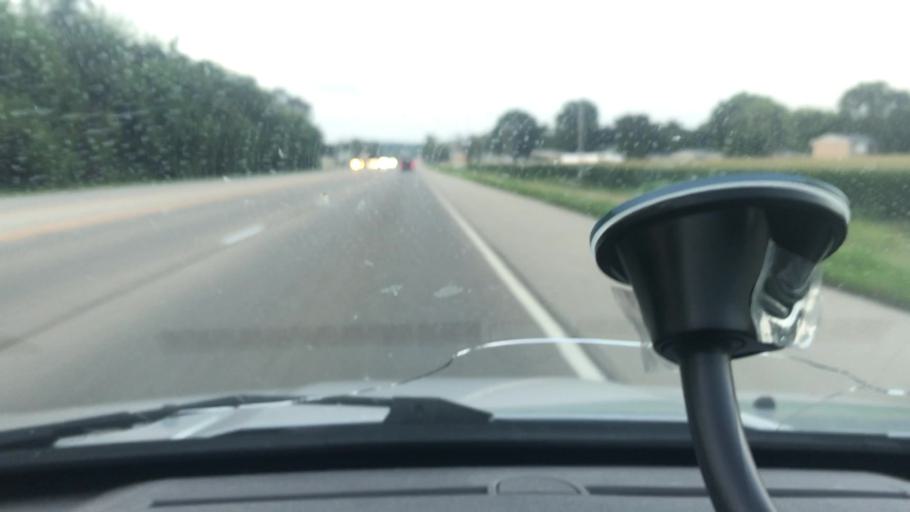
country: US
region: Illinois
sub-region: Tazewell County
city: North Pekin
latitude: 40.6153
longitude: -89.6293
